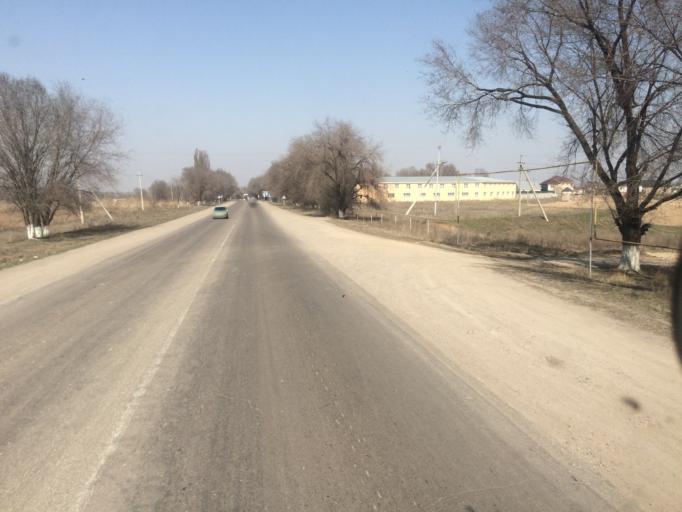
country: KZ
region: Almaty Oblysy
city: Burunday
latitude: 43.2973
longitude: 76.6729
